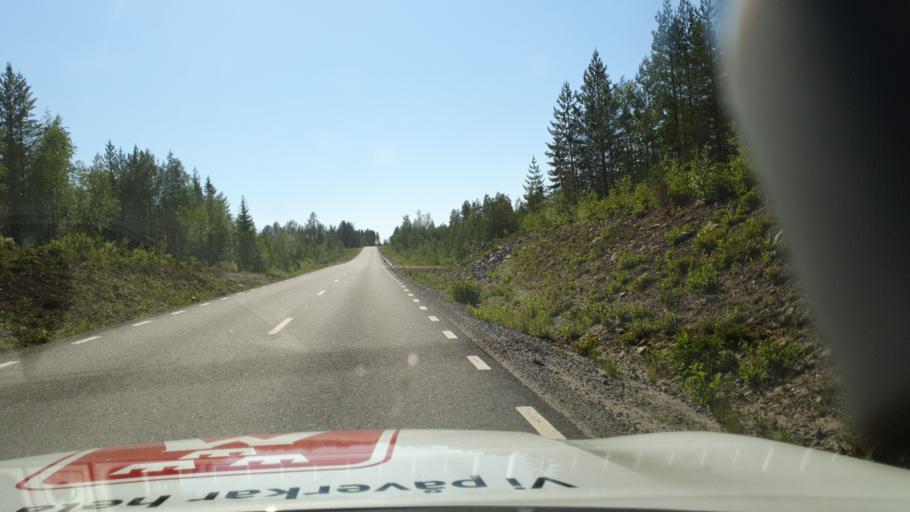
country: SE
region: Vaesterbotten
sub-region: Vindelns Kommun
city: Vindeln
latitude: 64.2486
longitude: 20.1104
